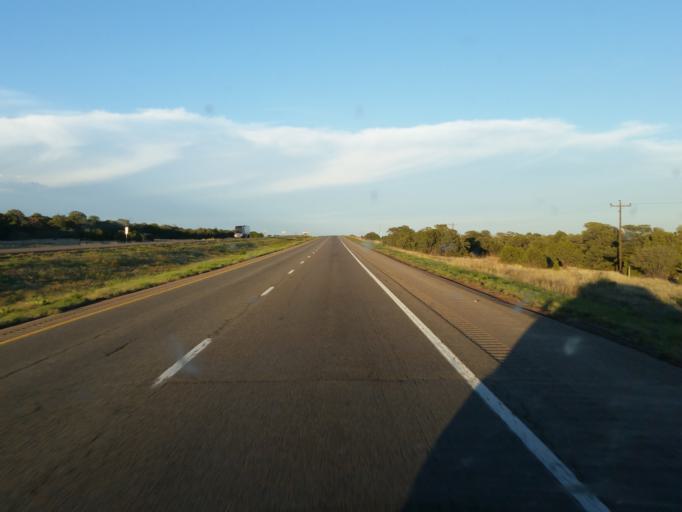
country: US
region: New Mexico
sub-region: Torrance County
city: Moriarty
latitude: 35.0043
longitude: -105.5969
